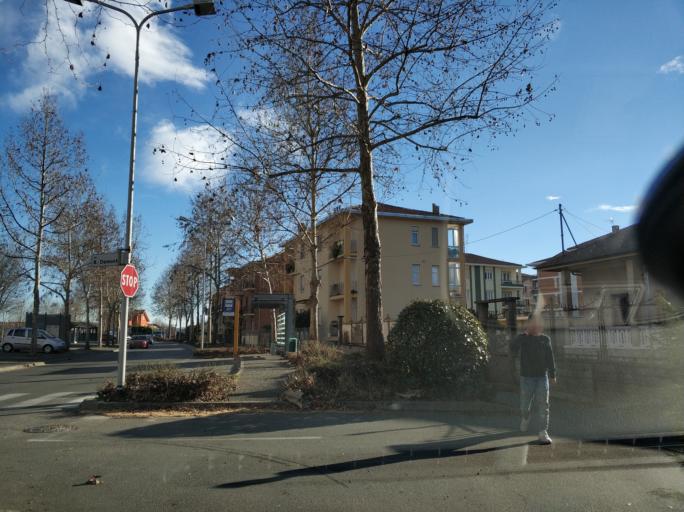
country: IT
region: Piedmont
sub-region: Provincia di Torino
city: Caselle Torinese
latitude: 45.1763
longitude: 7.6440
